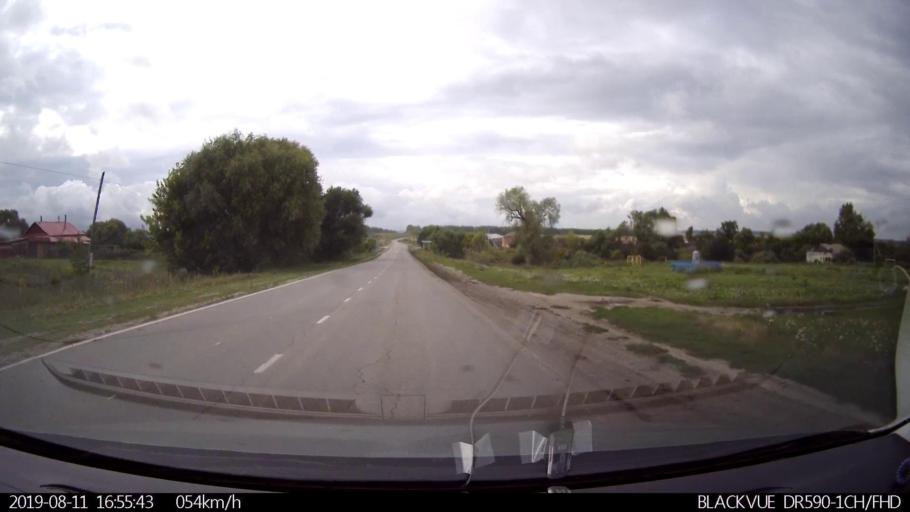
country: RU
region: Ulyanovsk
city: Mayna
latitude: 54.2835
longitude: 47.6609
